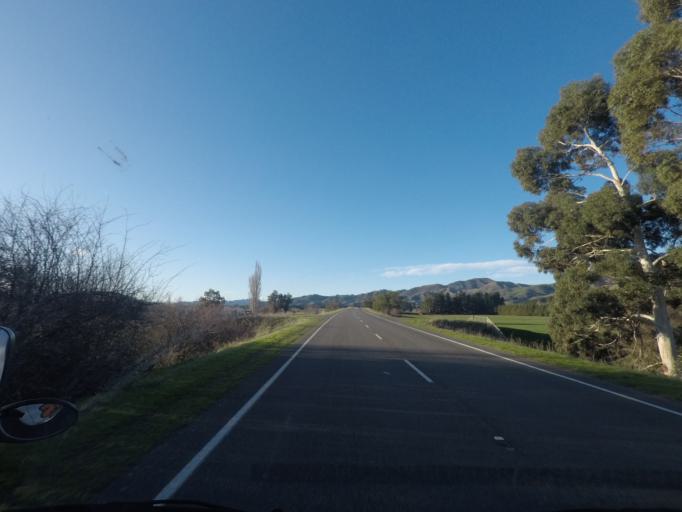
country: NZ
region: Canterbury
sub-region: Kaikoura District
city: Kaikoura
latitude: -42.7084
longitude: 173.2958
